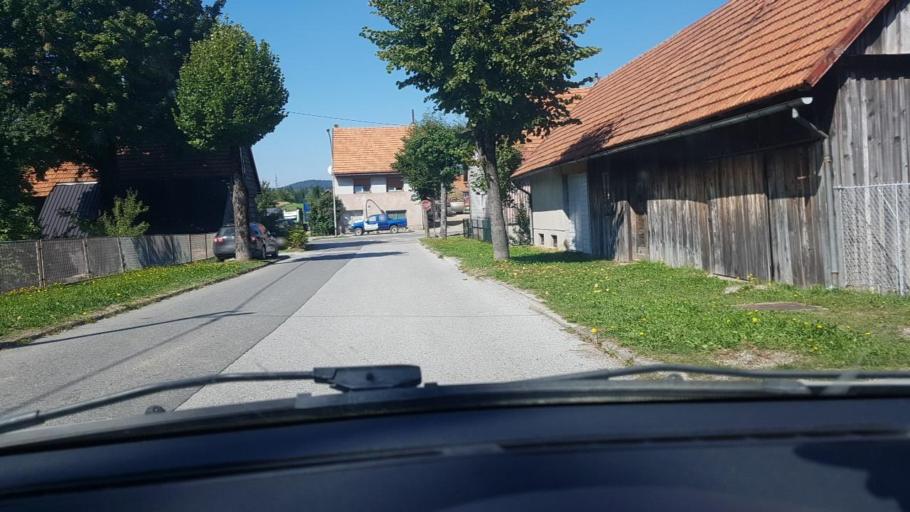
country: SI
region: Kostel
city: Kostel
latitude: 45.3732
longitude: 14.9387
